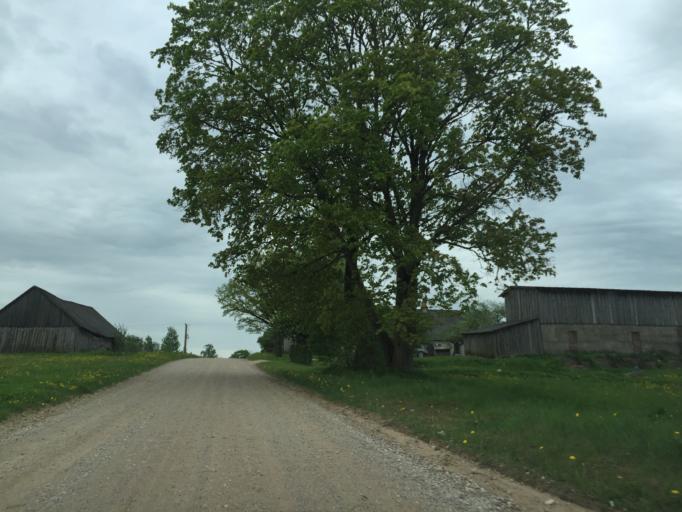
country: LV
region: Lielvarde
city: Lielvarde
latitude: 56.8067
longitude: 24.8322
